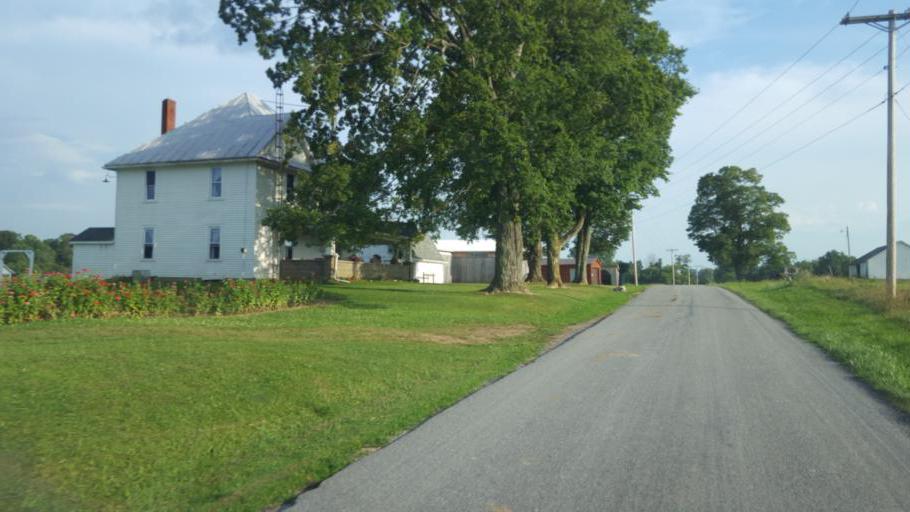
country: US
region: Ohio
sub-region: Knox County
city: Fredericktown
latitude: 40.5036
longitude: -82.6287
